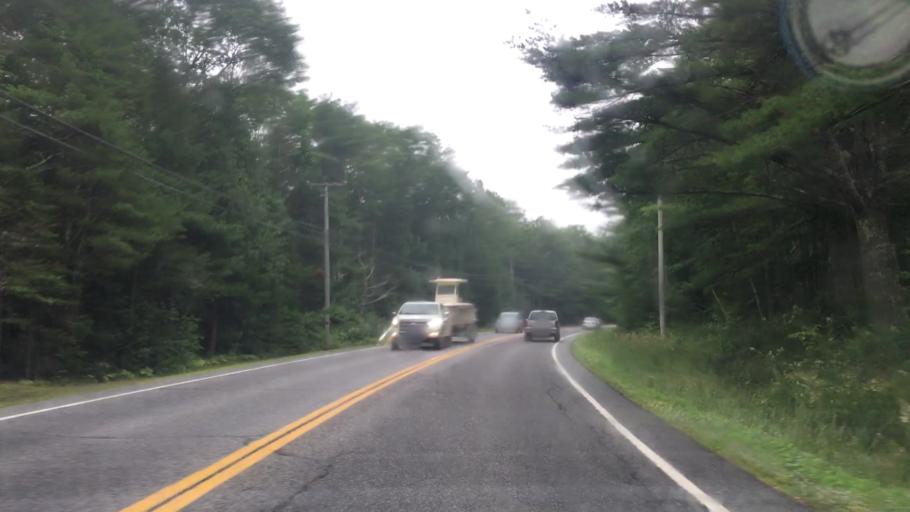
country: US
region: Maine
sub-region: Lincoln County
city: Edgecomb
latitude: 43.9292
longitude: -69.6163
